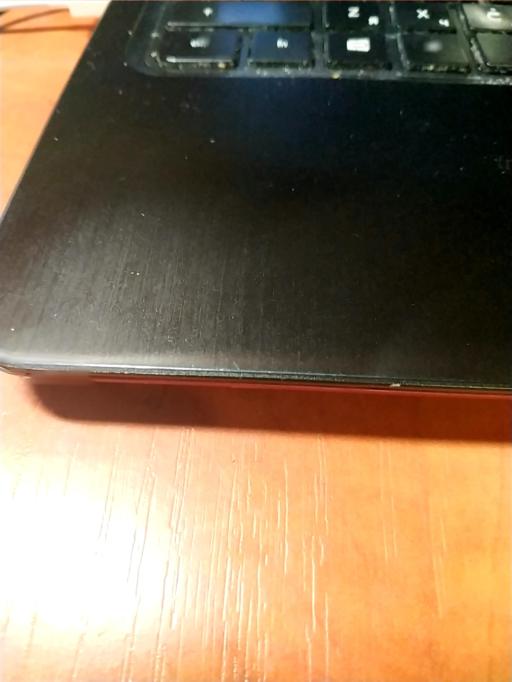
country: RU
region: Tverskaya
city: Likhoslavl'
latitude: 57.2275
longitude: 35.6000
